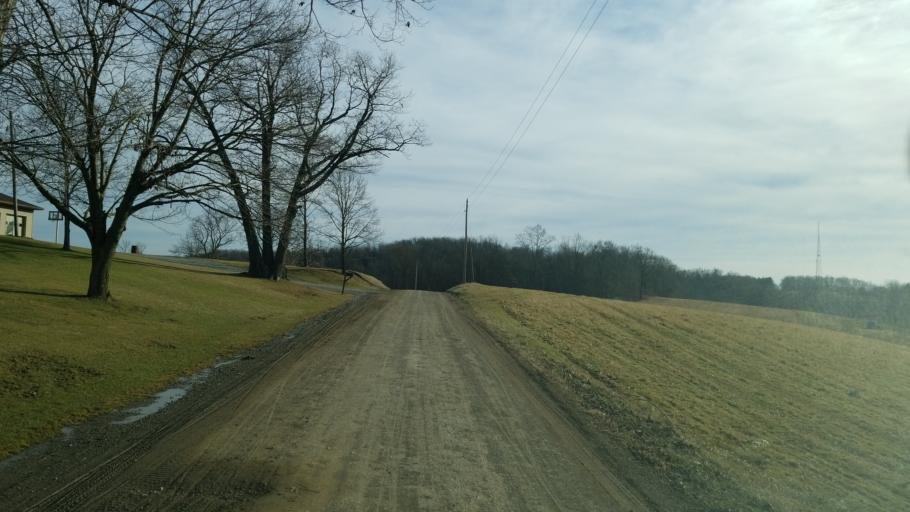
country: US
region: Pennsylvania
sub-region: Indiana County
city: Chevy Chase Heights
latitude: 40.8254
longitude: -79.1638
